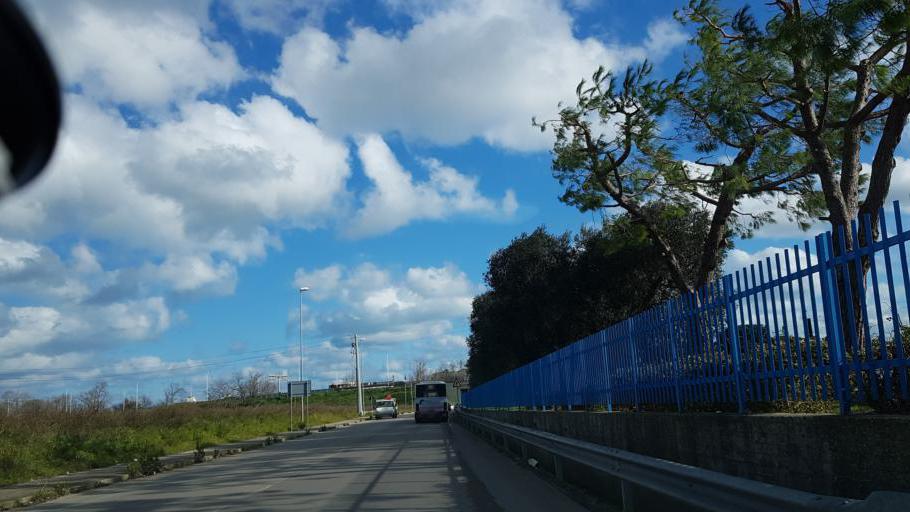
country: IT
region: Apulia
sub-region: Provincia di Brindisi
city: Brindisi
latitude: 40.6271
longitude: 17.9165
